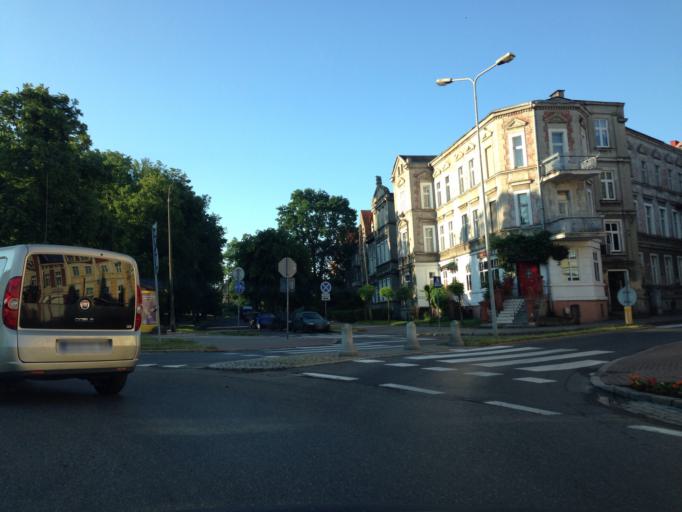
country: PL
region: Pomeranian Voivodeship
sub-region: Powiat kwidzynski
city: Kwidzyn
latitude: 53.7271
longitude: 18.9284
